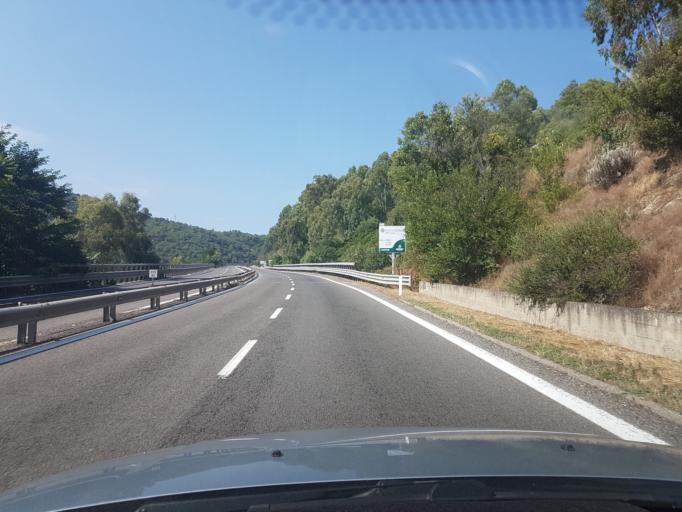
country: IT
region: Sardinia
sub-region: Provincia di Nuoro
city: Nuoro
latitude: 40.3382
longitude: 9.3014
